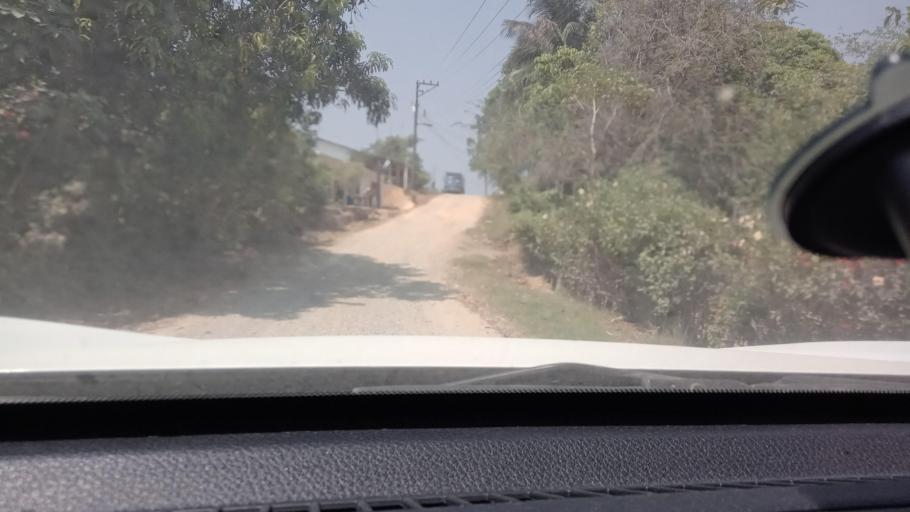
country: MX
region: Tabasco
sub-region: Huimanguillo
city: Francisco Rueda
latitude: 17.5067
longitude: -93.8999
